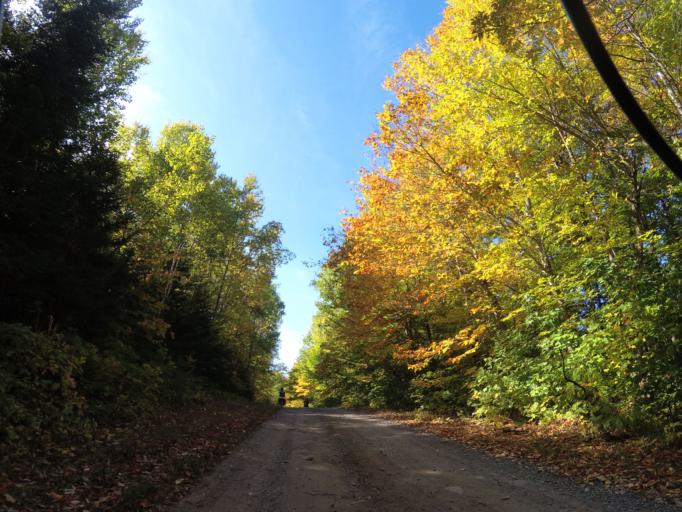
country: CA
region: Ontario
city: Renfrew
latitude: 45.3464
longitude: -77.0893
